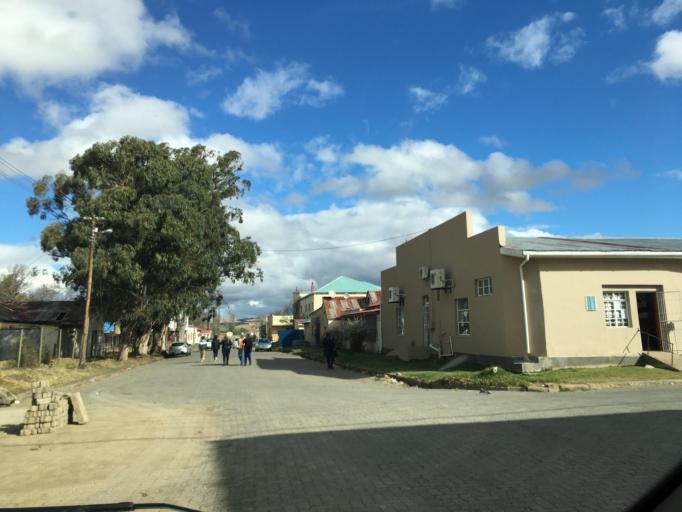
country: ZA
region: Eastern Cape
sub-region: Chris Hani District Municipality
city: Elliot
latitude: -31.3323
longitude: 27.8515
